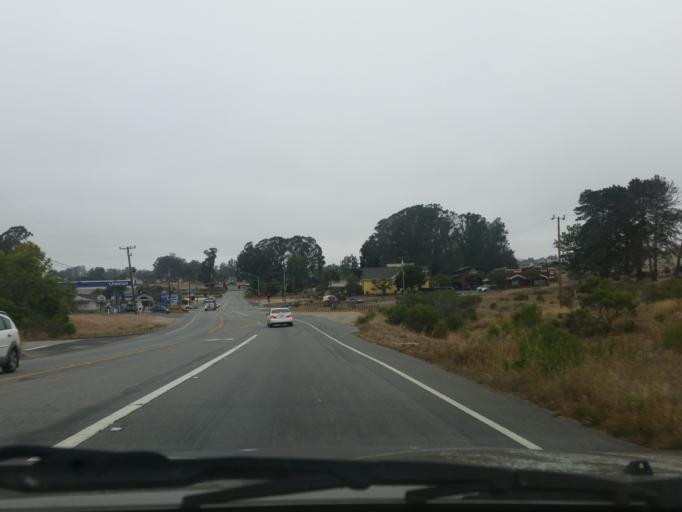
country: US
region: California
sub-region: San Luis Obispo County
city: Callender
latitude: 35.0793
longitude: -120.5881
